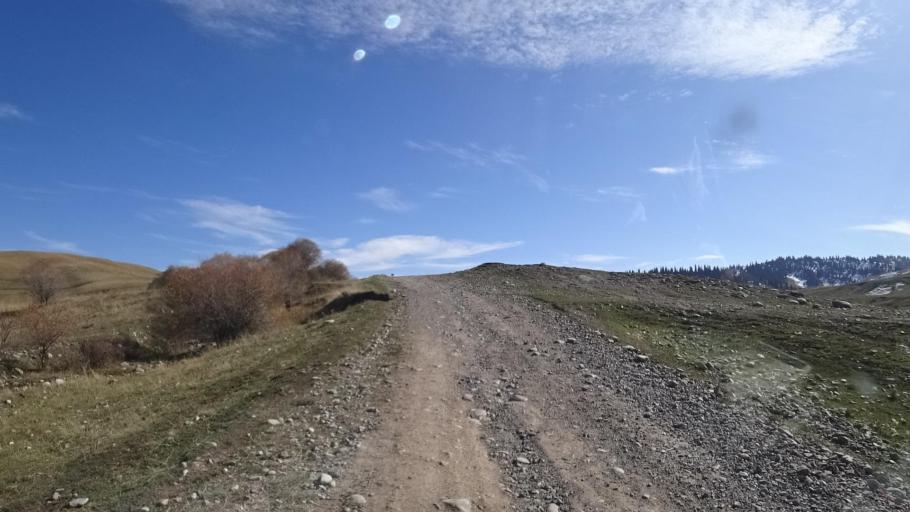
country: KZ
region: Almaty Oblysy
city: Kegen
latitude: 42.7366
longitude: 79.0152
